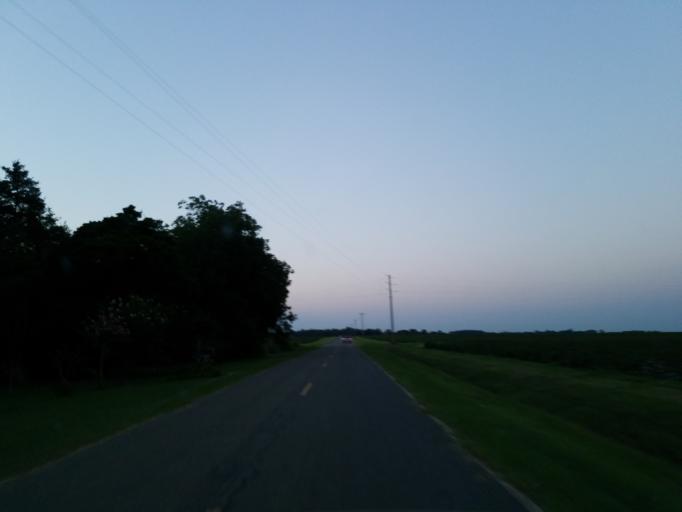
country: US
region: Georgia
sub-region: Dooly County
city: Unadilla
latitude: 32.2740
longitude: -83.7962
